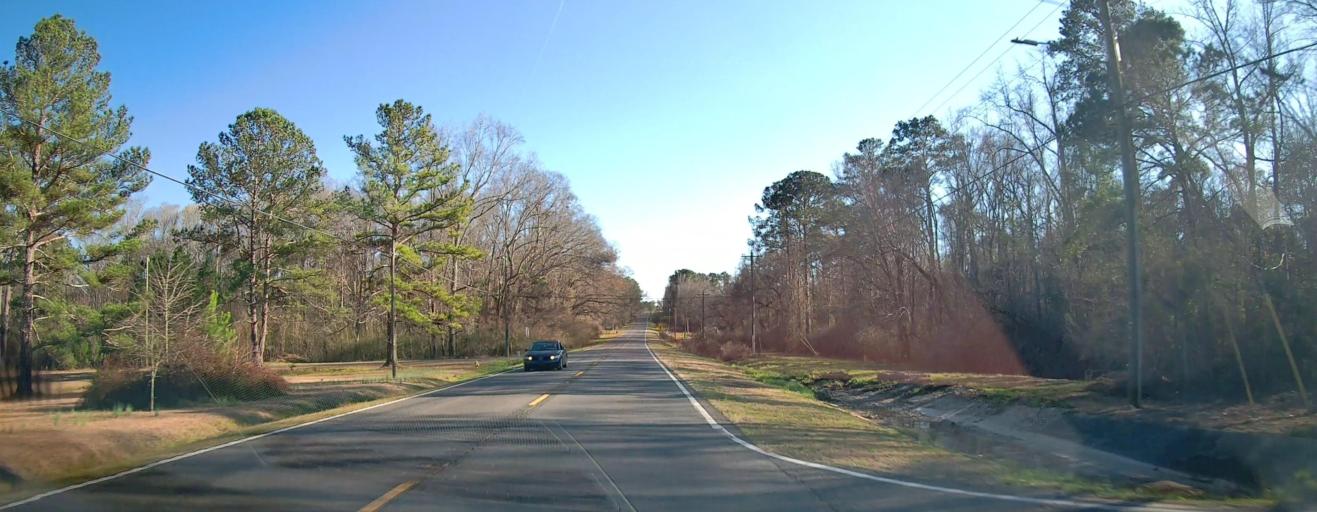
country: US
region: Georgia
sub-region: Sumter County
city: Americus
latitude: 32.0409
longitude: -84.2216
